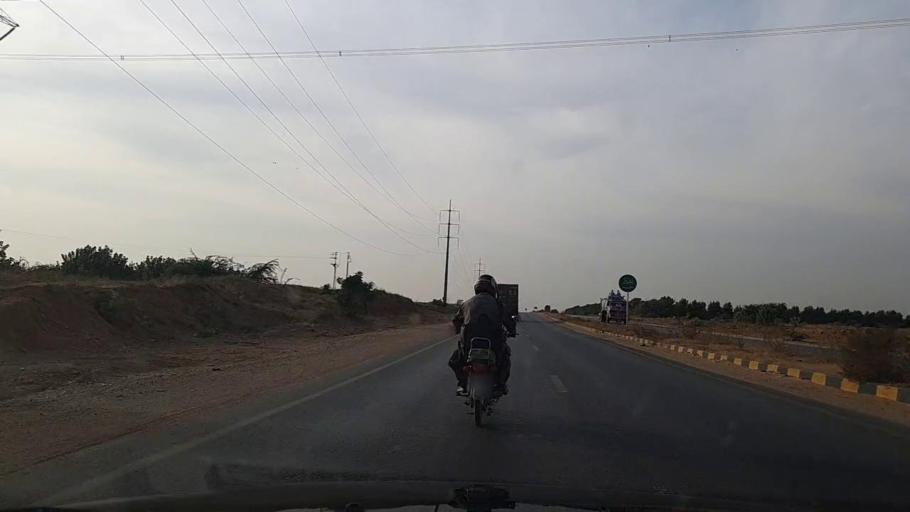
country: PK
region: Sindh
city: Gharo
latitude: 24.8196
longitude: 67.4856
